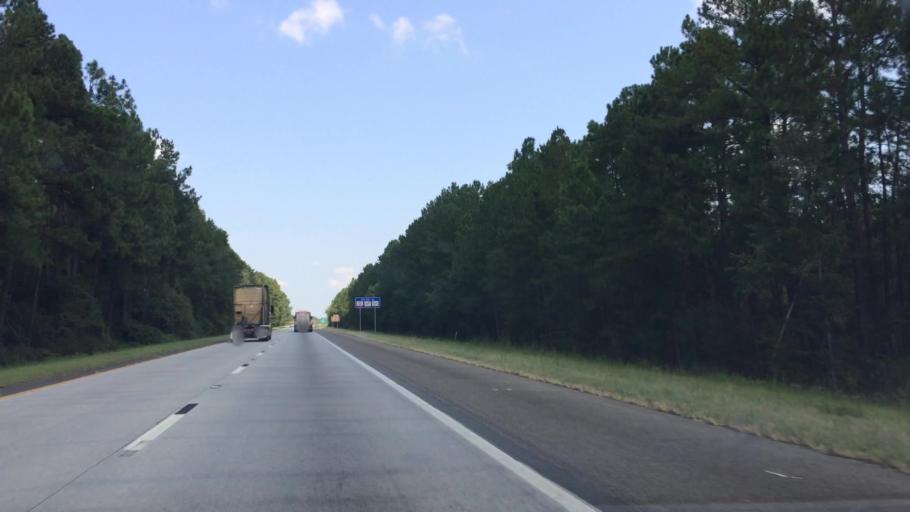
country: US
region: South Carolina
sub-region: Dorchester County
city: Saint George
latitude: 33.0723
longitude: -80.6581
